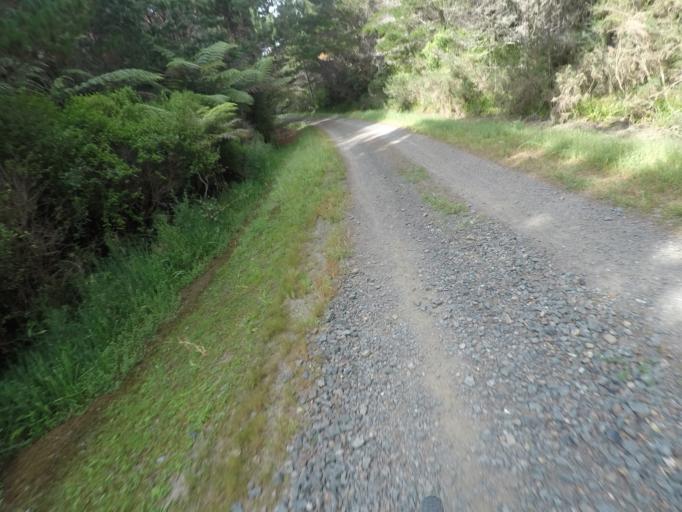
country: NZ
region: Auckland
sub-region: Auckland
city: Muriwai Beach
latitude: -36.7445
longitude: 174.5657
